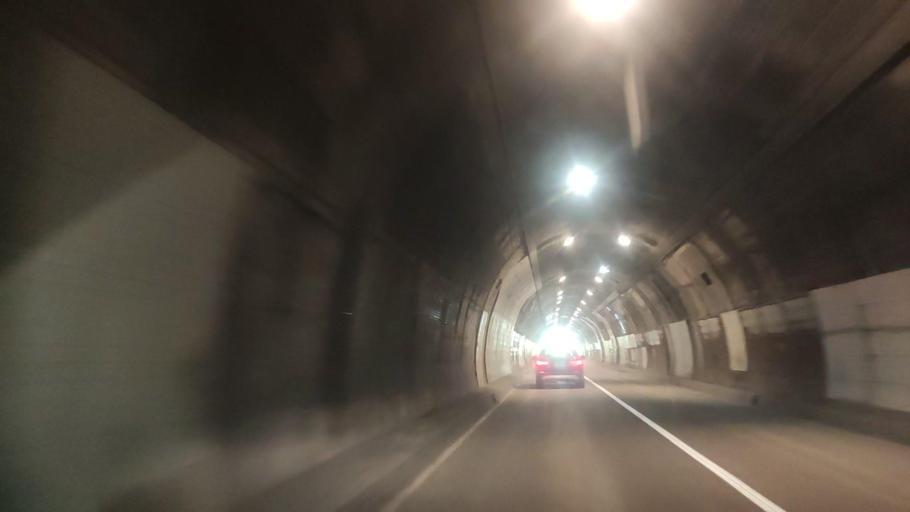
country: JP
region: Hokkaido
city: Date
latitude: 42.5637
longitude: 140.7401
